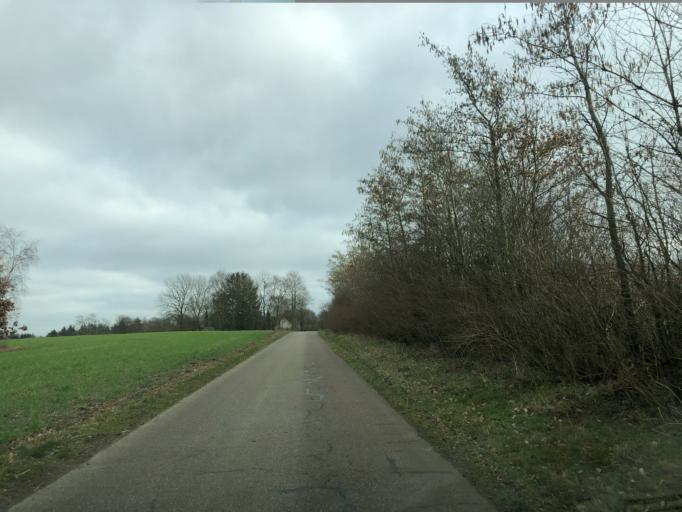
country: DK
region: South Denmark
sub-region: Billund Kommune
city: Billund
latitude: 55.7833
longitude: 9.1578
